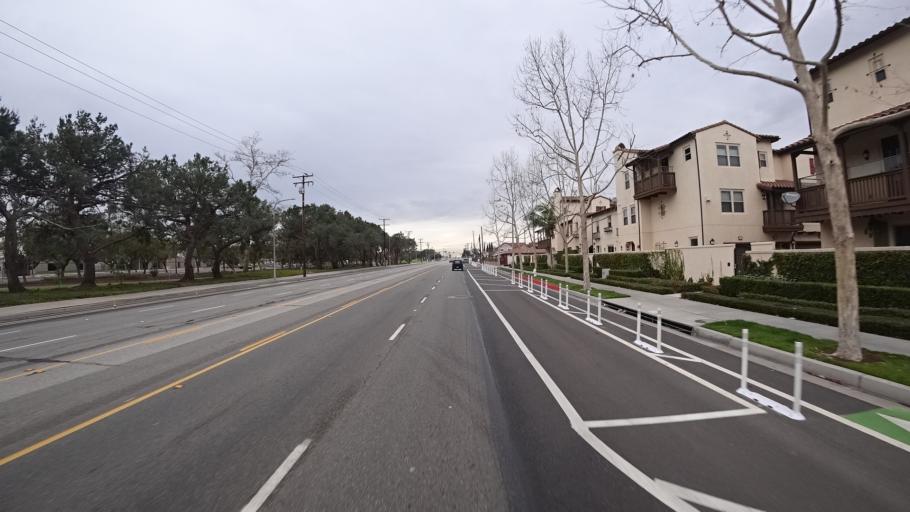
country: US
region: California
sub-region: Orange County
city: Santa Ana
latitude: 33.7277
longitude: -117.9088
